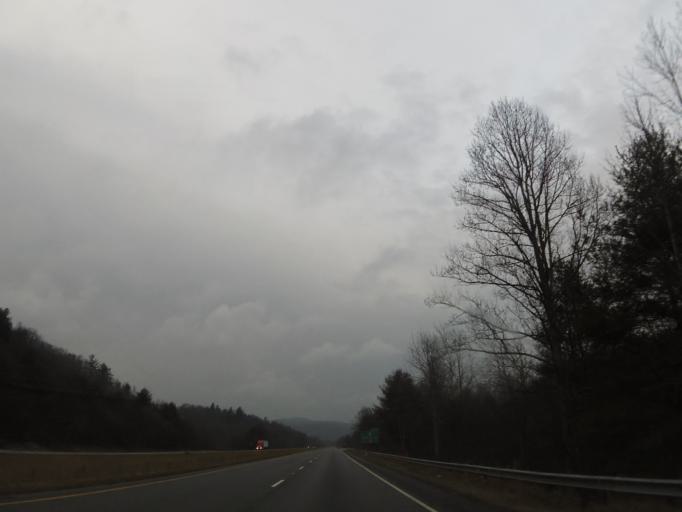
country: US
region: North Carolina
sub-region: Henderson County
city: Flat Rock
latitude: 35.1832
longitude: -82.4474
